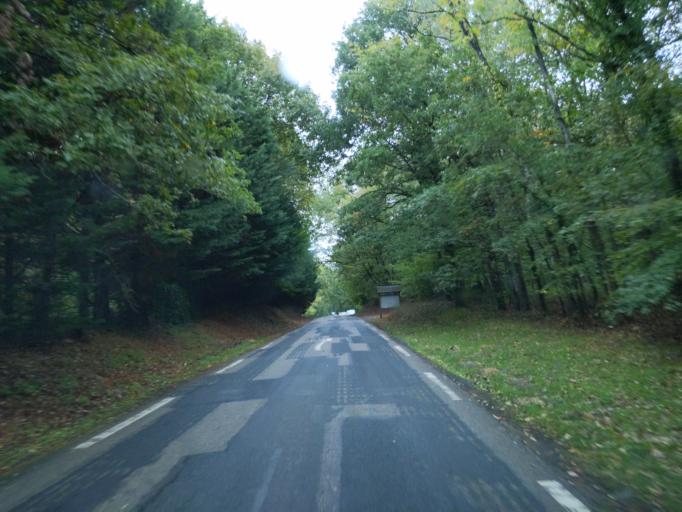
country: FR
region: Ile-de-France
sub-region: Departement des Yvelines
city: Bullion
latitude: 48.5921
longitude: 1.9919
